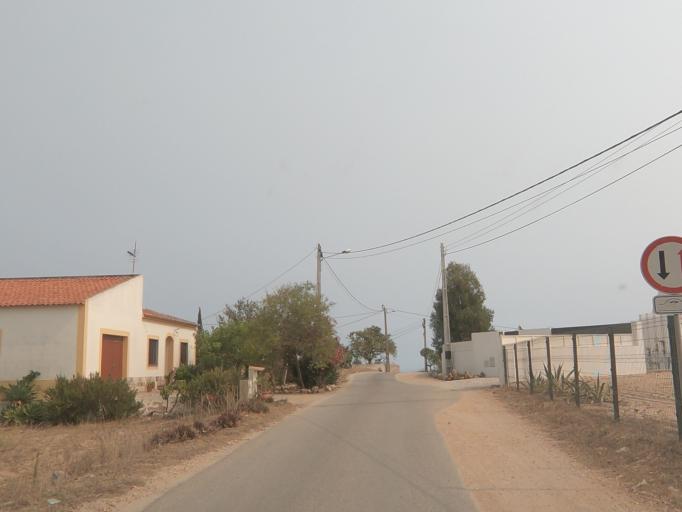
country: PT
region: Faro
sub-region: Lagoa
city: Carvoeiro
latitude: 37.0999
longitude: -8.4124
